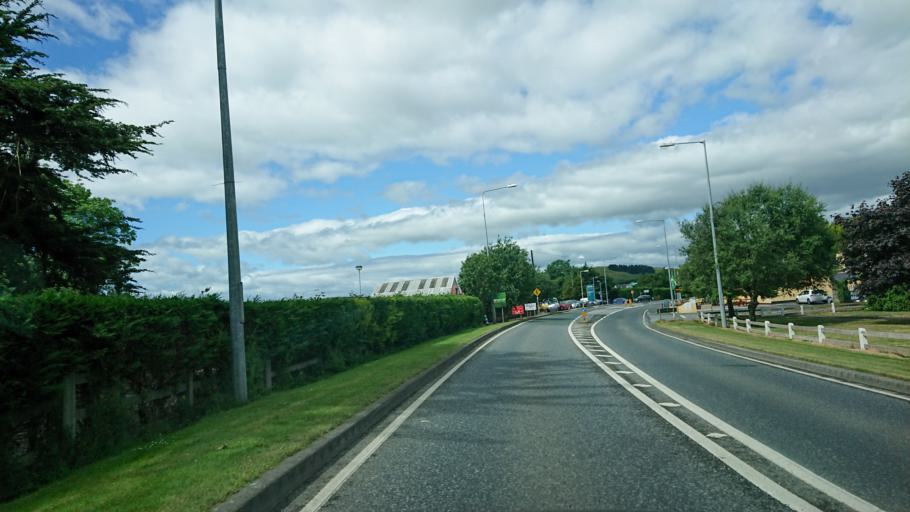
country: IE
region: Leinster
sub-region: Kilkenny
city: Mooncoin
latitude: 52.2274
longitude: -7.2304
